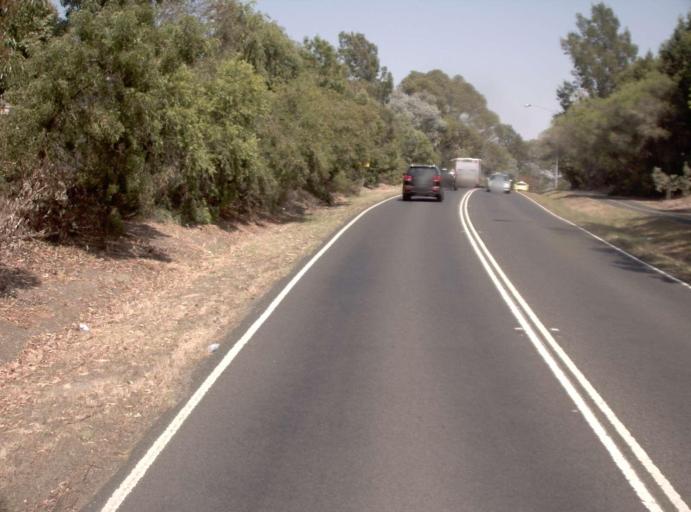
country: AU
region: Victoria
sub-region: Manningham
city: Doncaster East
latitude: -37.7734
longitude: 145.1441
